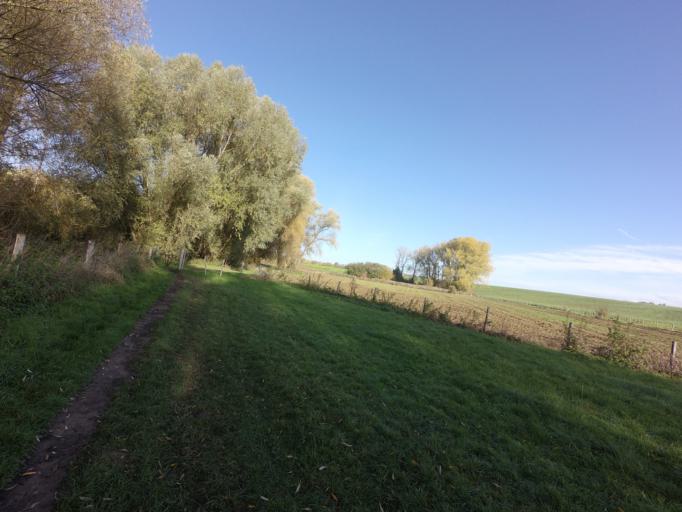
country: NL
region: Limburg
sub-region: Gemeente Voerendaal
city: Ubachsberg
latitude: 50.8009
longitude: 5.9190
